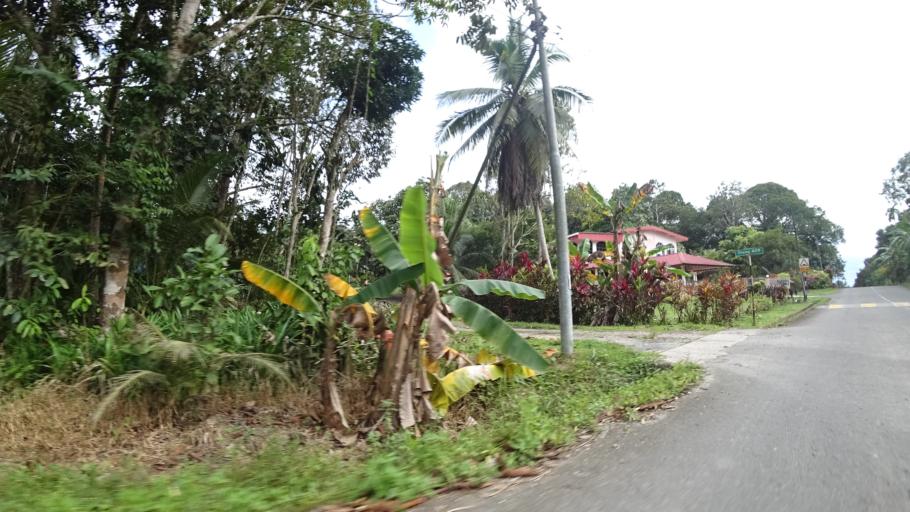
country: MY
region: Sarawak
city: Limbang
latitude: 4.8260
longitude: 114.9479
